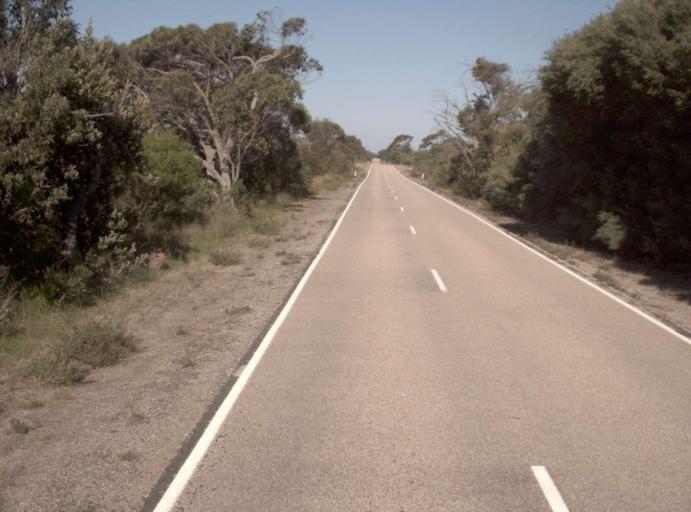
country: AU
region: Victoria
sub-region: East Gippsland
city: Lakes Entrance
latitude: -37.8009
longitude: 148.6440
